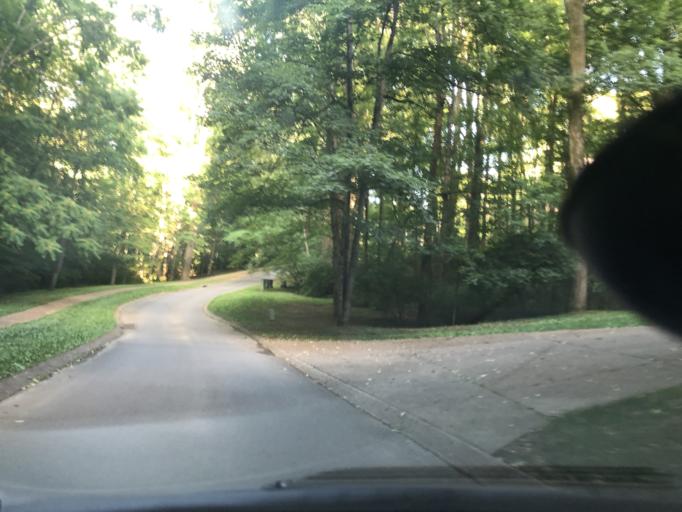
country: US
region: Tennessee
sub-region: Davidson County
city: Forest Hills
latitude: 36.0530
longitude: -86.8345
